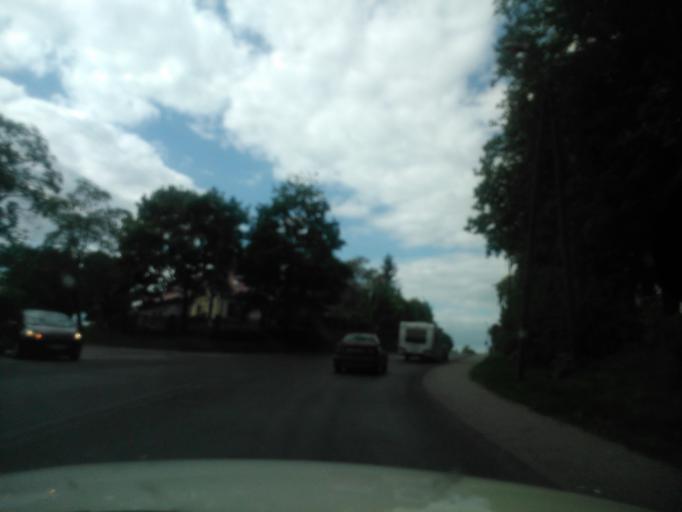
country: PL
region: Masovian Voivodeship
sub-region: Powiat radomski
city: Ilza
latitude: 51.1650
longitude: 21.2331
